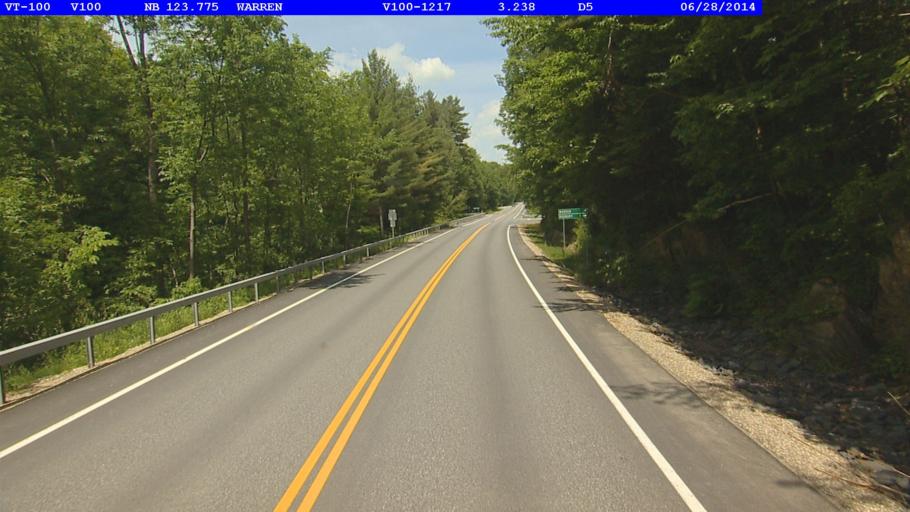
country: US
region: Vermont
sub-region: Washington County
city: Northfield
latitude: 44.1051
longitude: -72.8602
